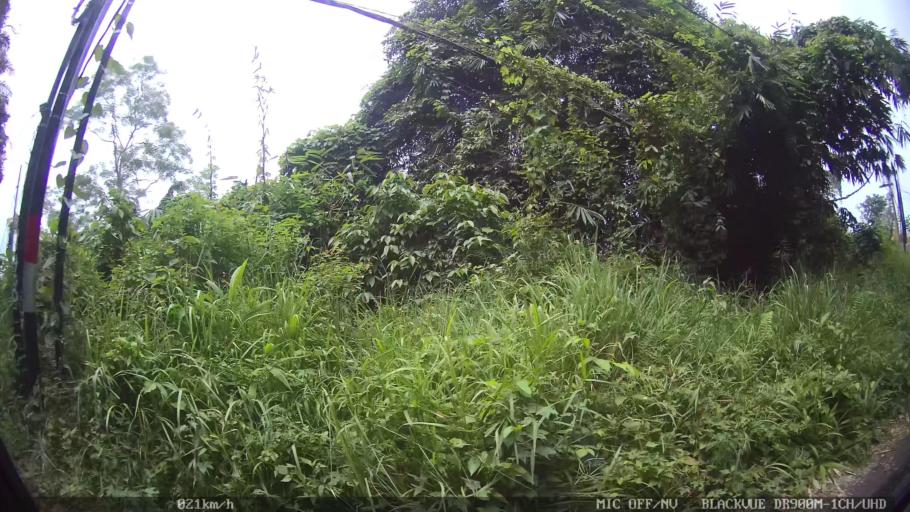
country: ID
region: Lampung
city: Panjang
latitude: -5.4360
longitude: 105.3098
